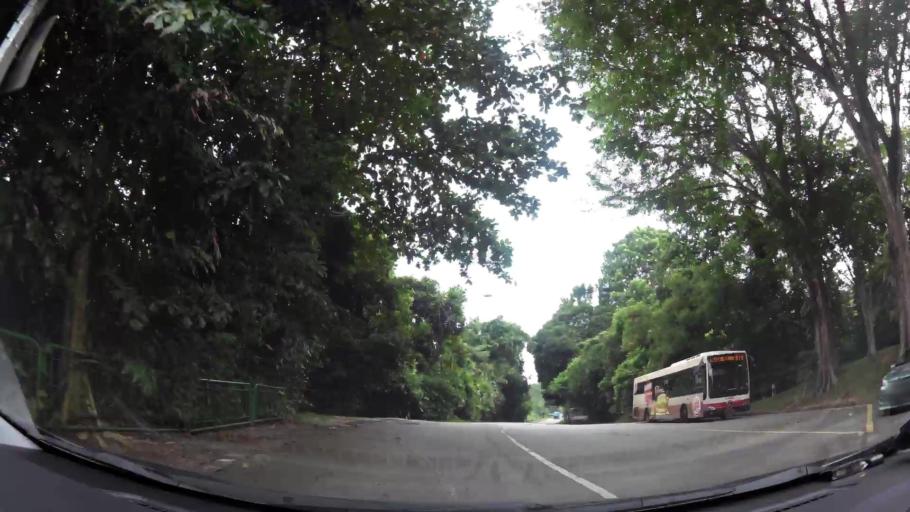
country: MY
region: Johor
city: Johor Bahru
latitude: 1.4449
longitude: 103.7076
